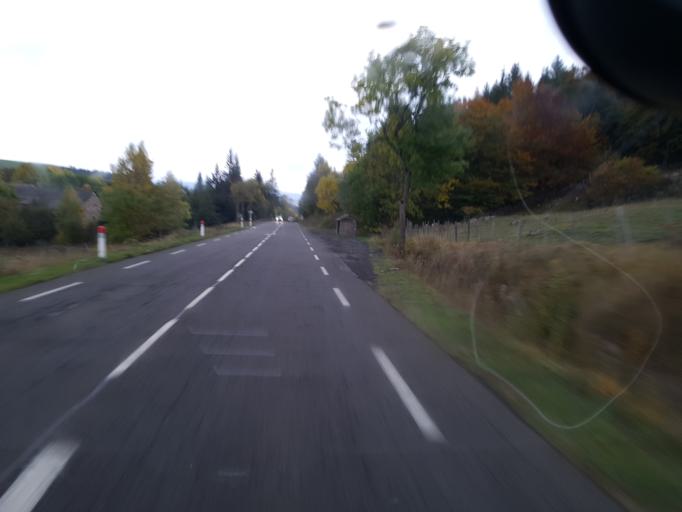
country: FR
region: Languedoc-Roussillon
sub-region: Departement de la Lozere
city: Mende
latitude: 44.5545
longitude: 3.6247
